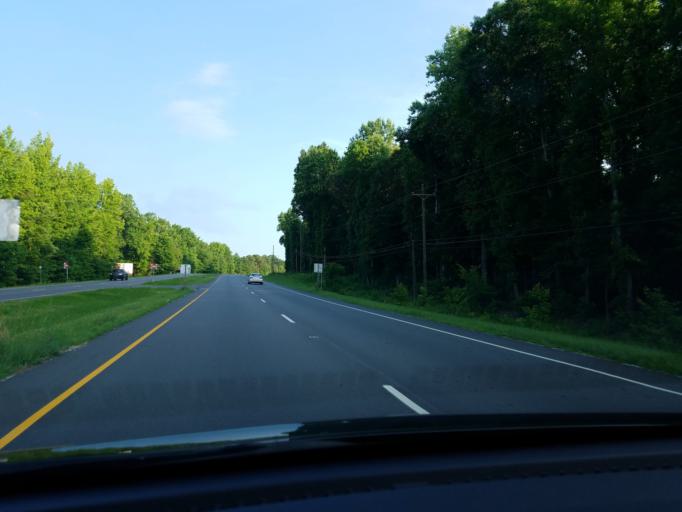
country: US
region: North Carolina
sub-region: Durham County
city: Gorman
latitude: 36.1293
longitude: -78.9026
